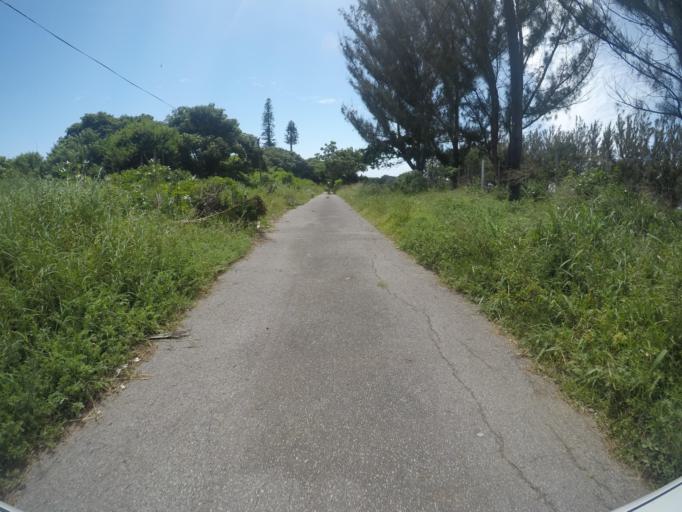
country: ZA
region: Eastern Cape
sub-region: Buffalo City Metropolitan Municipality
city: East London
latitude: -32.9527
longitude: 28.0011
